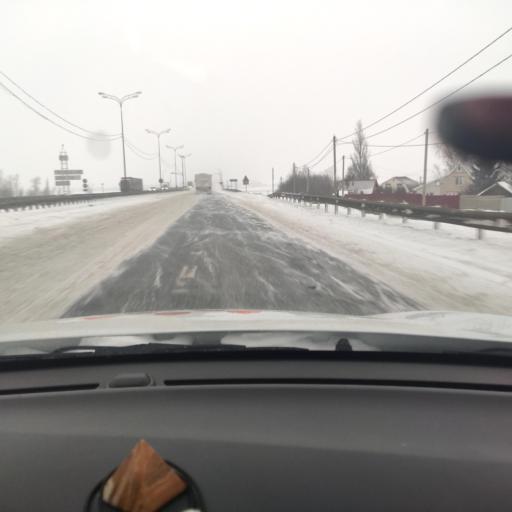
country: RU
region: Tatarstan
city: Osinovo
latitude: 55.7793
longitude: 48.8404
